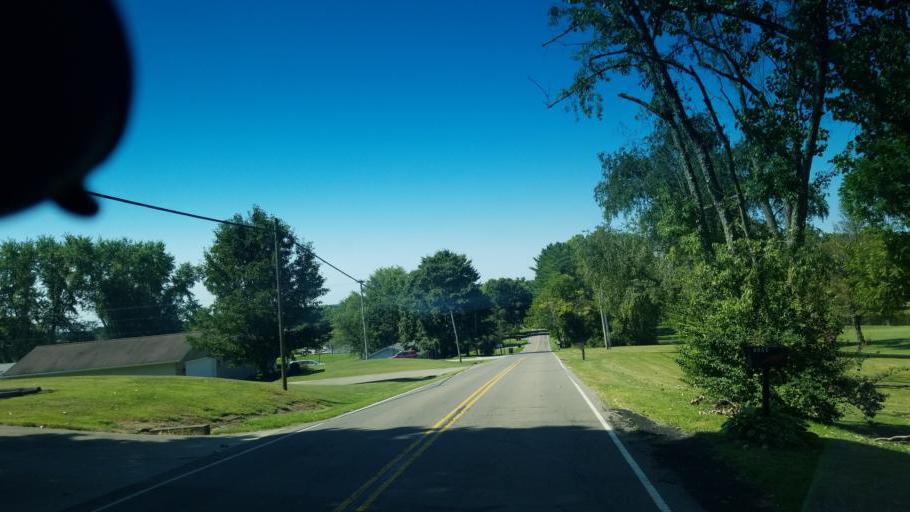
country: US
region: Ohio
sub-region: Licking County
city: Newark
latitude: 40.1133
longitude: -82.4033
